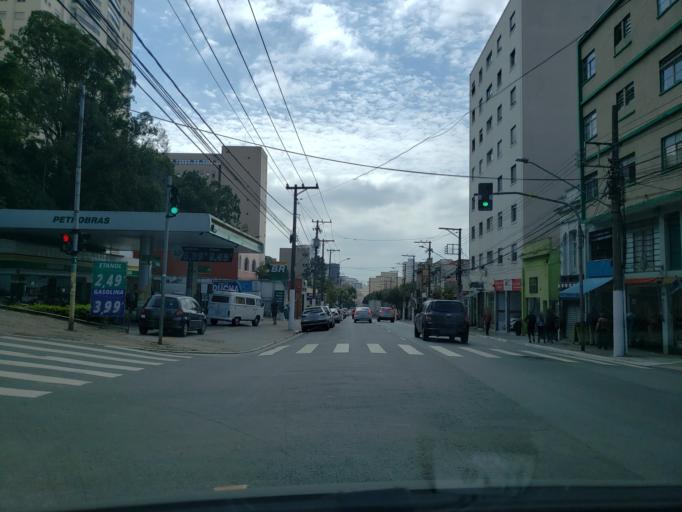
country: BR
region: Sao Paulo
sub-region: Sao Paulo
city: Sao Paulo
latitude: -23.5679
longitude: -46.6218
